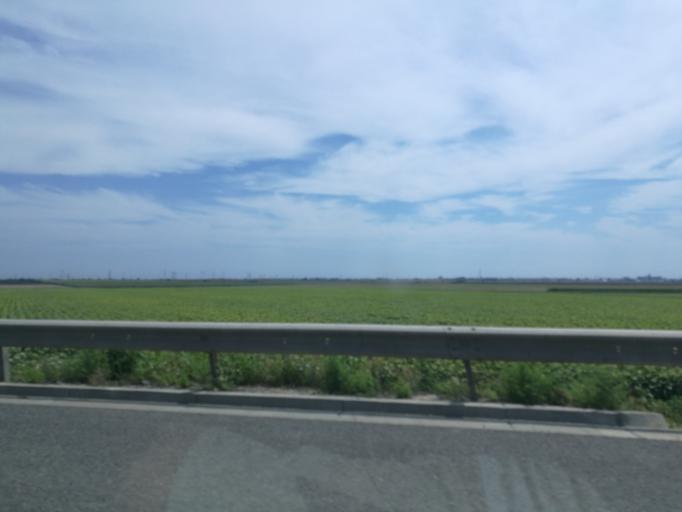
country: RO
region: Constanta
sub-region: Municipiul Constanta
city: Palazu Mare
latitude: 44.1940
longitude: 28.5517
